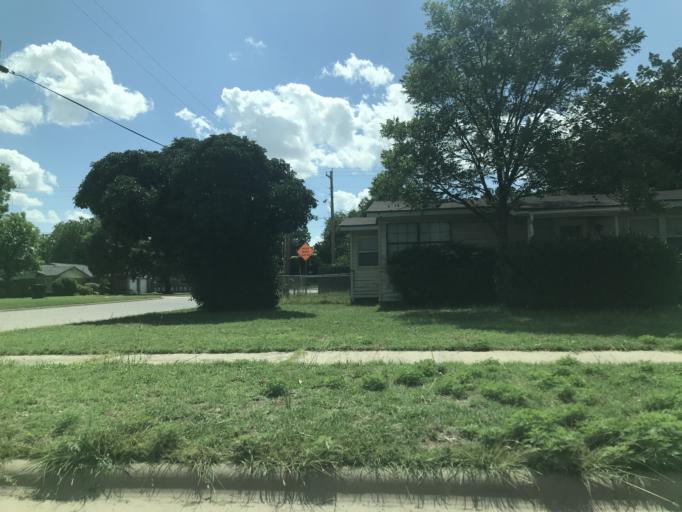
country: US
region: Texas
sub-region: Taylor County
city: Abilene
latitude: 32.4254
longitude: -99.7624
